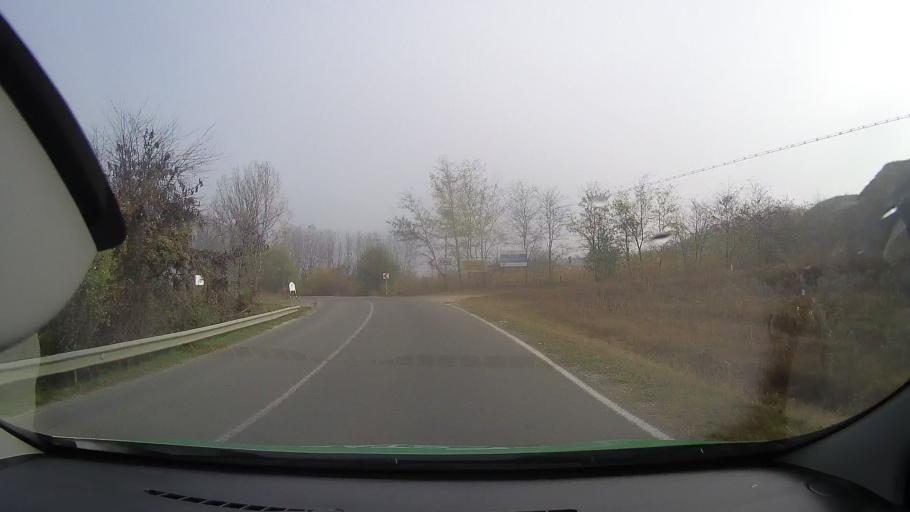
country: RO
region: Tulcea
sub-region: Comuna Nufaru
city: Nufaru
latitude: 45.1477
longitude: 28.9132
